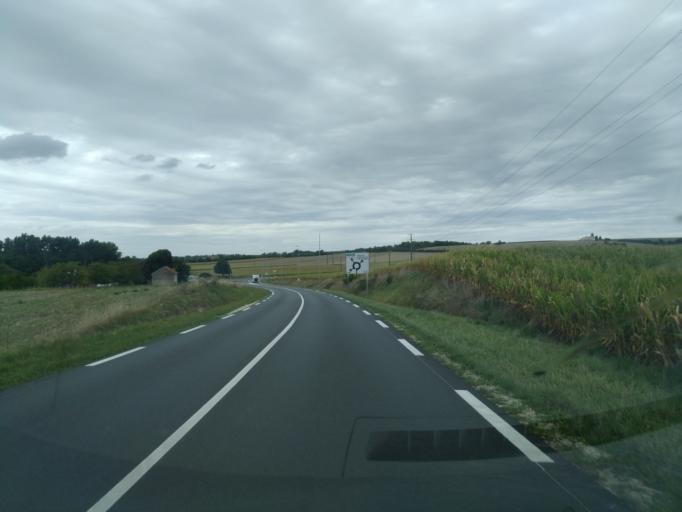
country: FR
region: Poitou-Charentes
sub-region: Departement de la Charente-Maritime
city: Pons
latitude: 45.5775
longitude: -0.5291
